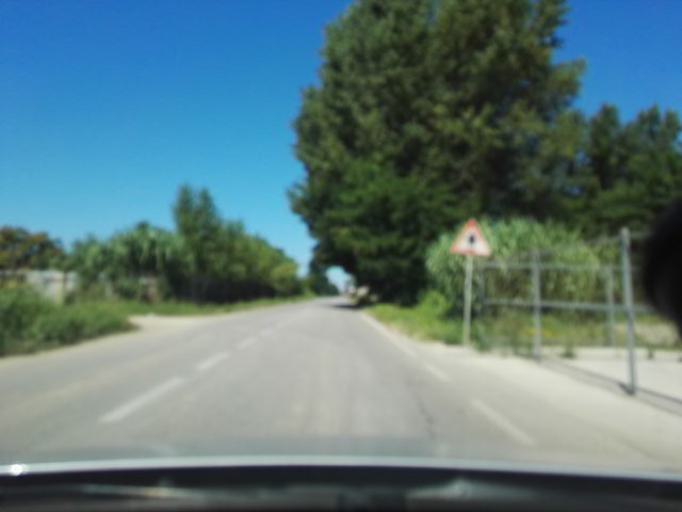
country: IT
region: Campania
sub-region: Provincia di Caserta
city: Casapesenna
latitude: 40.9853
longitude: 14.1409
